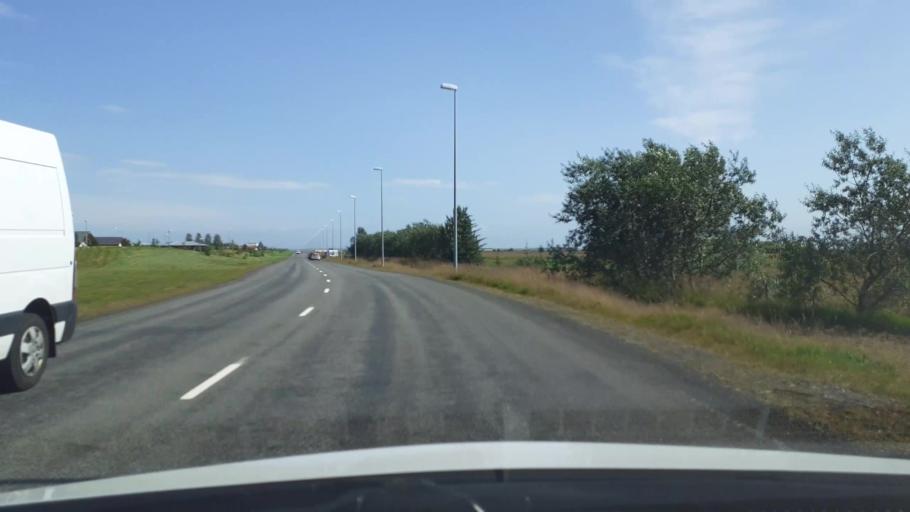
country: IS
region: South
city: Selfoss
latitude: 63.9224
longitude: -21.0045
